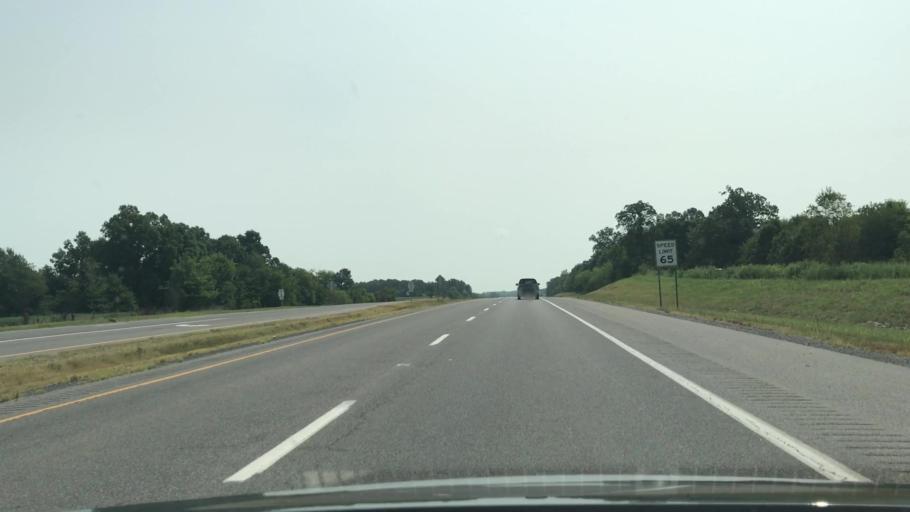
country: US
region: Kentucky
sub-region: Calloway County
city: Murray
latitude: 36.6510
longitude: -88.2713
